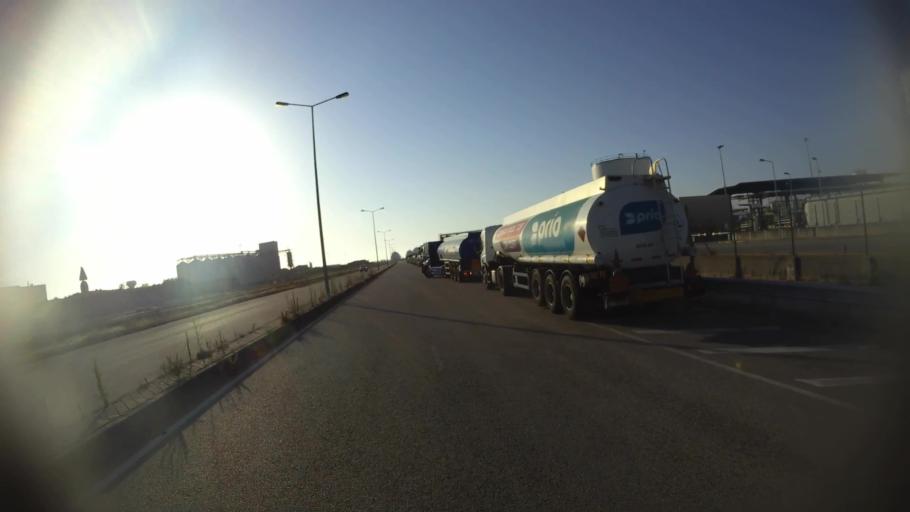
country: PT
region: Aveiro
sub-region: Ilhavo
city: Gafanha da Nazare
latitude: 40.6514
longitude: -8.7058
